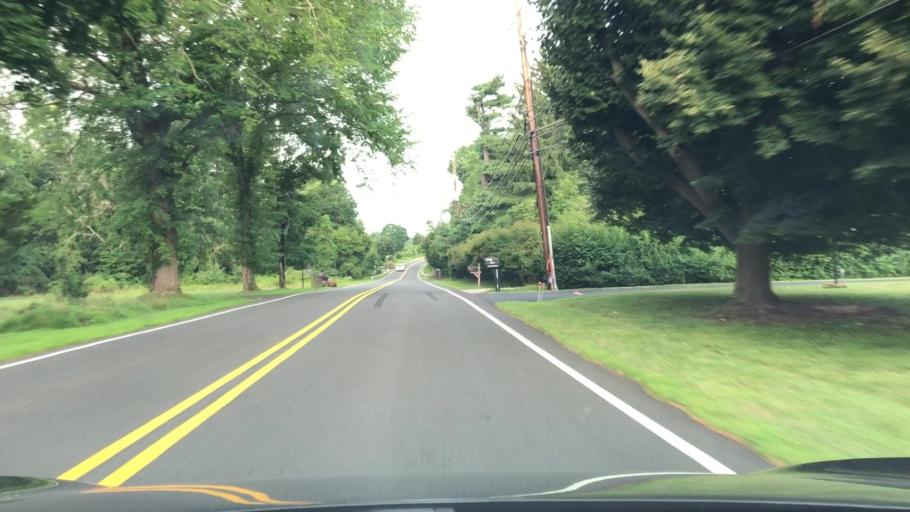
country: US
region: New Jersey
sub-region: Mercer County
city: Pennington
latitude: 40.3381
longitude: -74.7611
